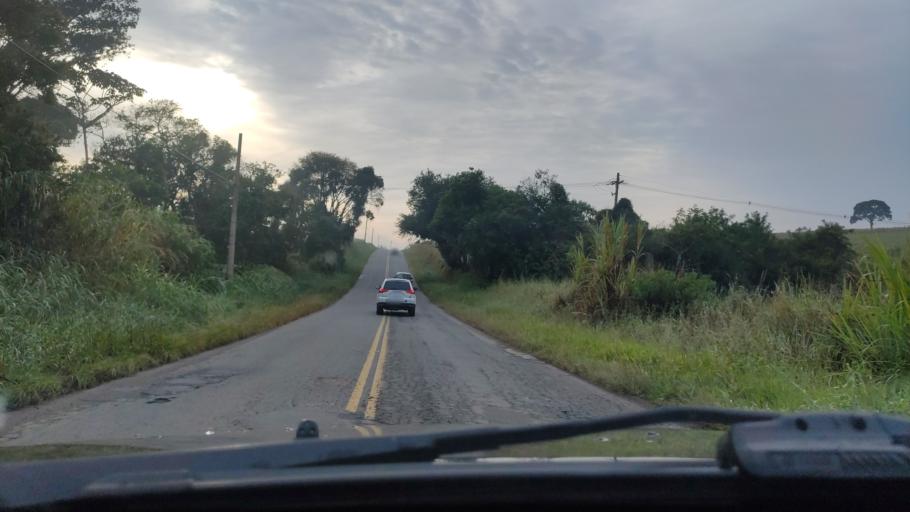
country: BR
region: Sao Paulo
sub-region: Jarinu
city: Jarinu
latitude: -23.1342
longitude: -46.7831
